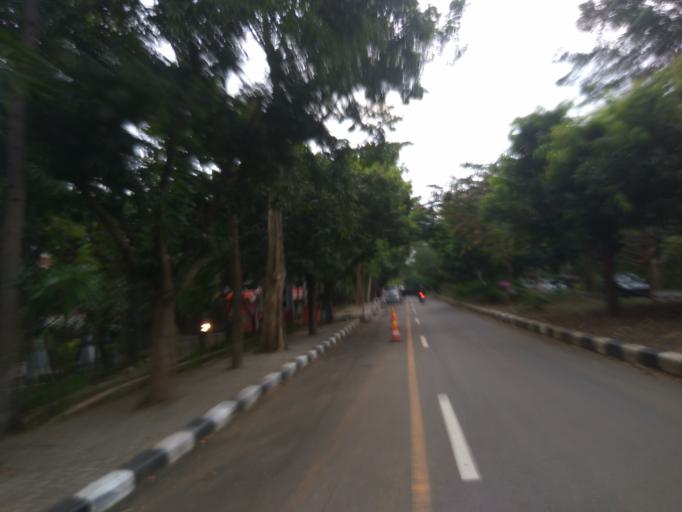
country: ID
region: Central Java
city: Semarang
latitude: -7.0508
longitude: 110.4369
